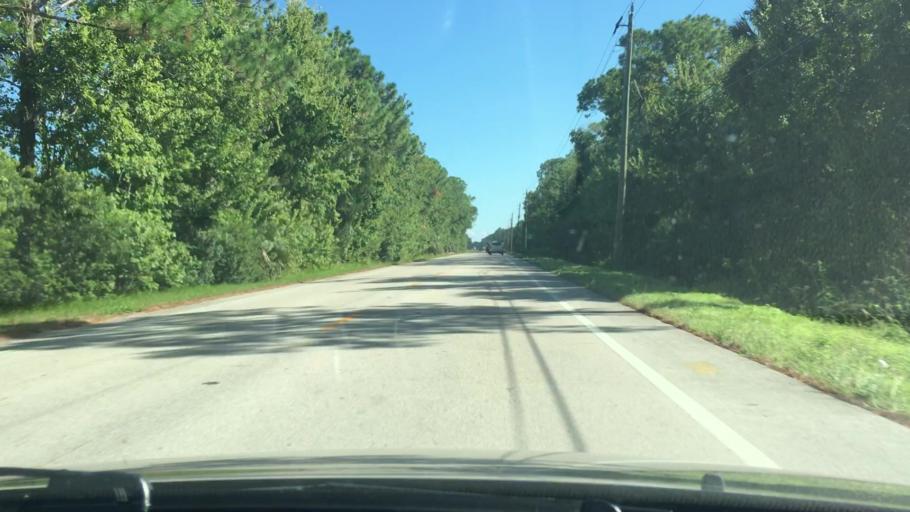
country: US
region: Florida
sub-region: Volusia County
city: South Daytona
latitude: 29.1384
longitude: -81.0772
